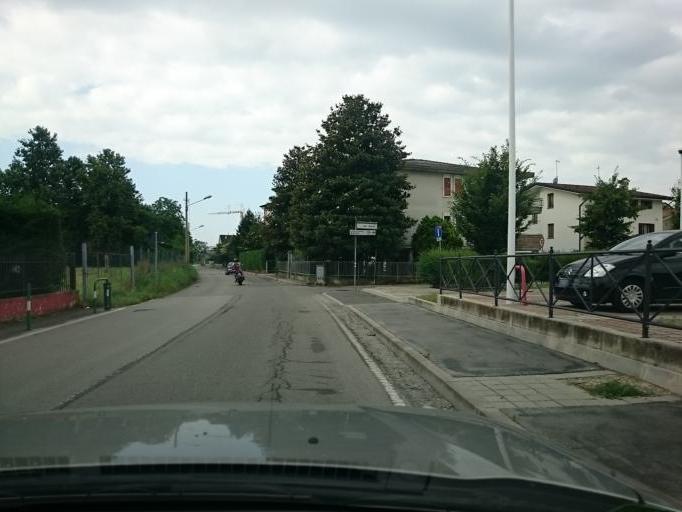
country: IT
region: Veneto
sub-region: Provincia di Padova
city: Padova
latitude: 45.3819
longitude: 11.8789
